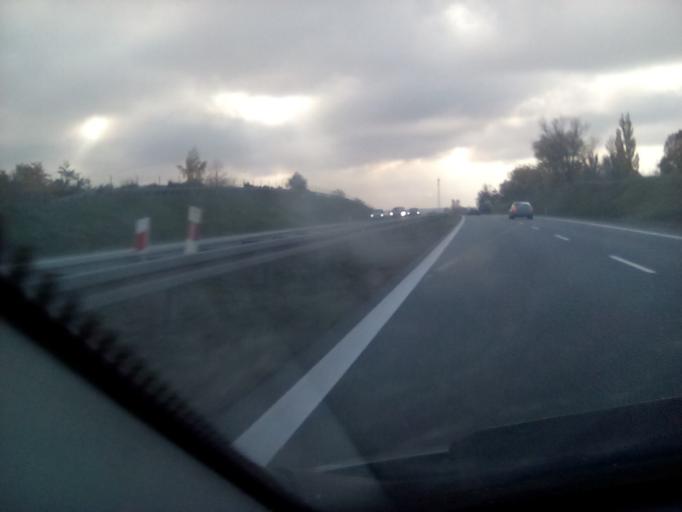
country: PL
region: Masovian Voivodeship
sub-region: Powiat bialobrzeski
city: Promna
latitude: 51.6836
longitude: 20.9371
